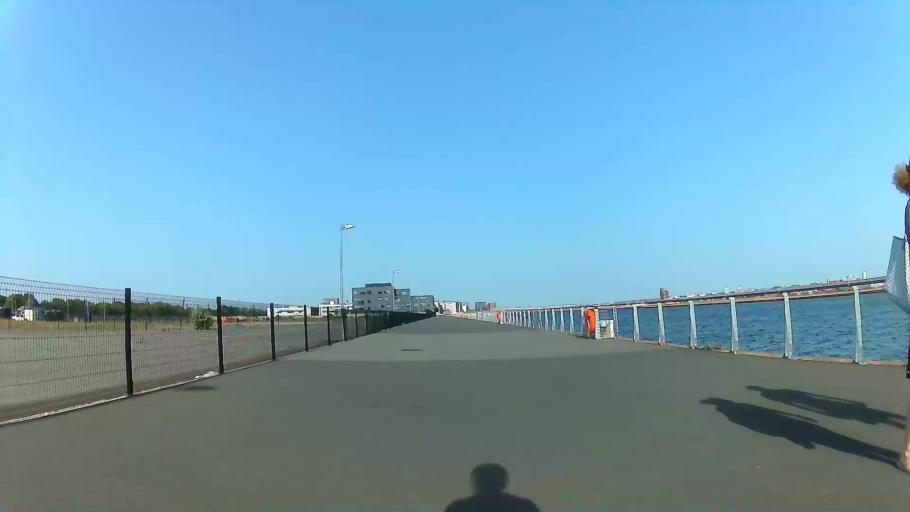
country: GB
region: England
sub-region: Greater London
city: Woolwich
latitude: 51.5073
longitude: 0.0554
